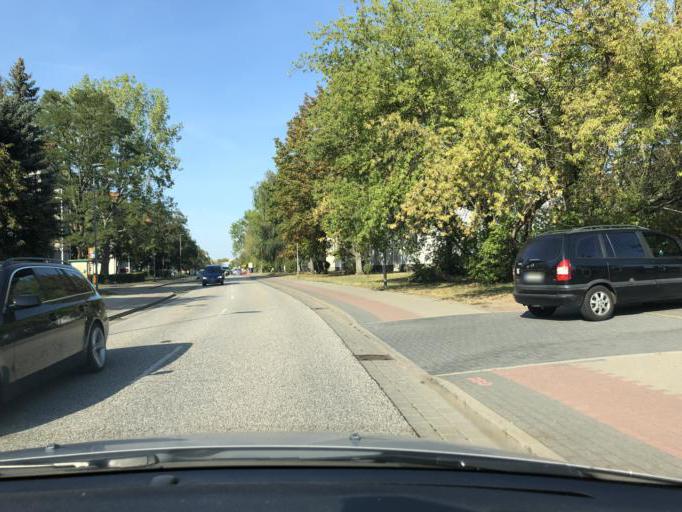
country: DE
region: Saxony-Anhalt
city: Zscherben
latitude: 51.3307
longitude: 11.9809
